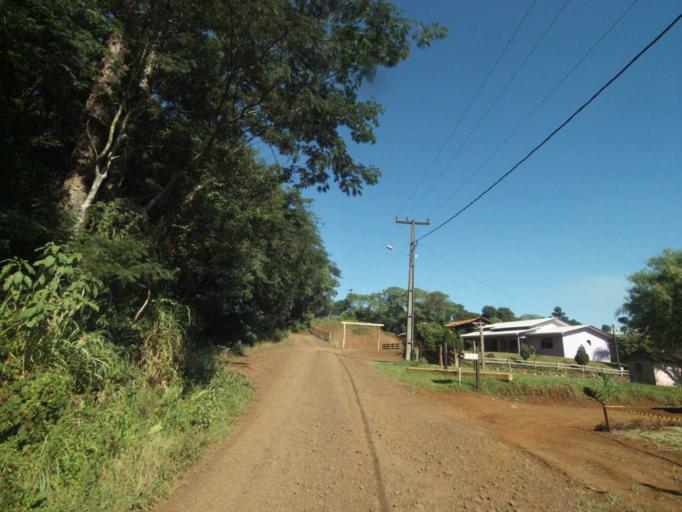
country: BR
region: Parana
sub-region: Laranjeiras Do Sul
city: Laranjeiras do Sul
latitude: -25.3793
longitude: -52.1946
